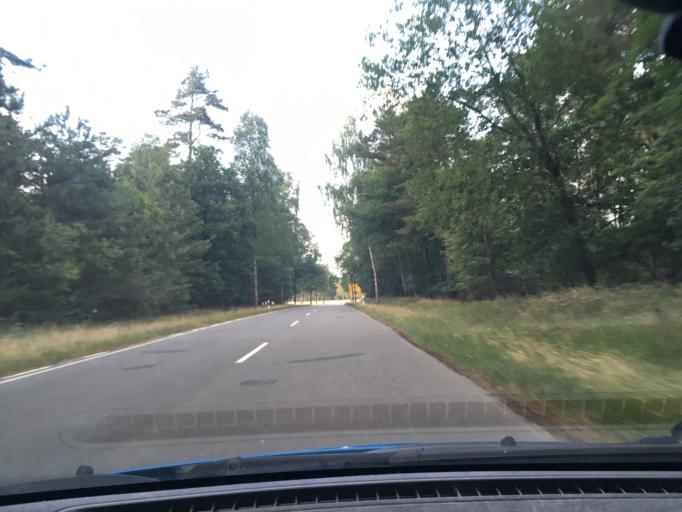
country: DE
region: Lower Saxony
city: Bispingen
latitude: 53.1182
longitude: 9.9461
